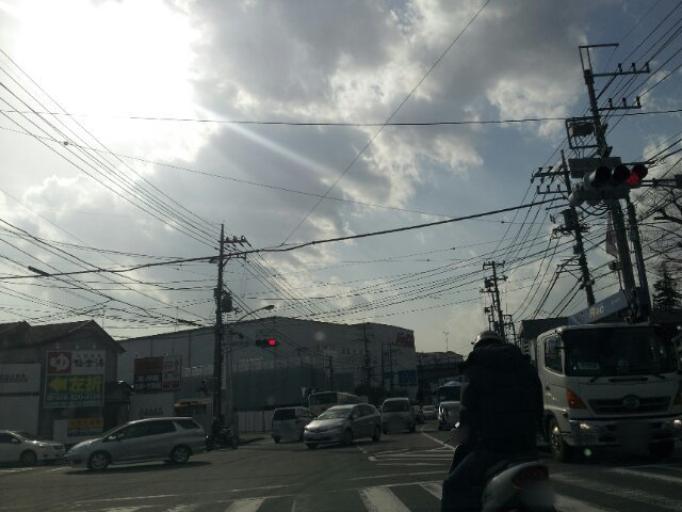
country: JP
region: Kanagawa
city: Yokohama
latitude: 35.4203
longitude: 139.5624
